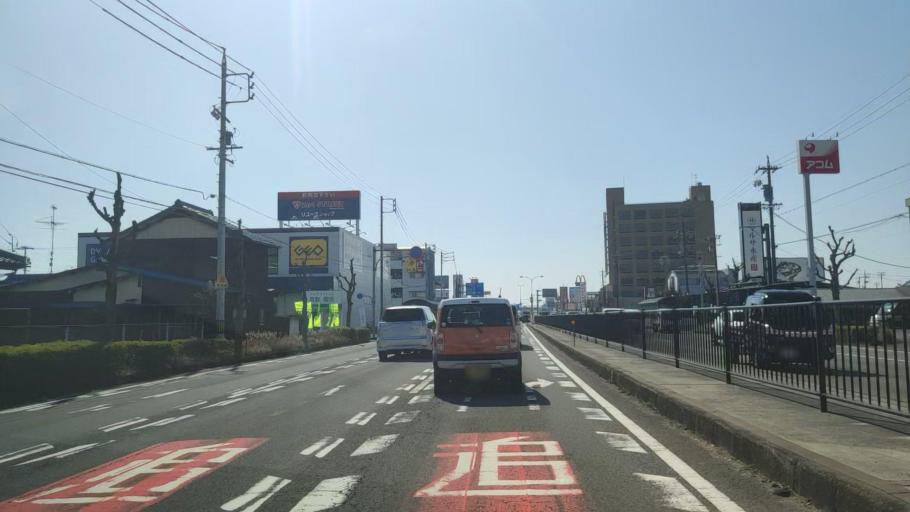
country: JP
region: Gifu
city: Kasamatsucho
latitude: 35.3954
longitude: 136.7853
